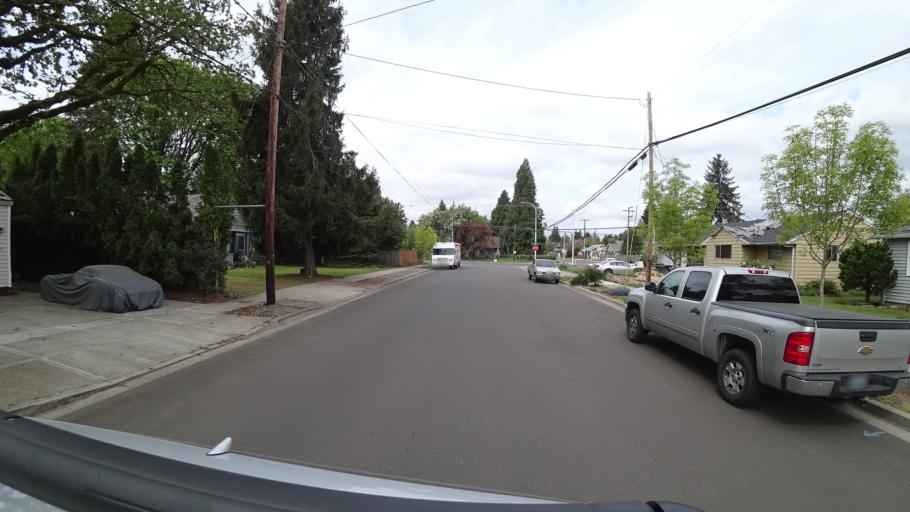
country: US
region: Oregon
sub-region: Washington County
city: Hillsboro
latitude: 45.5277
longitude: -122.9930
